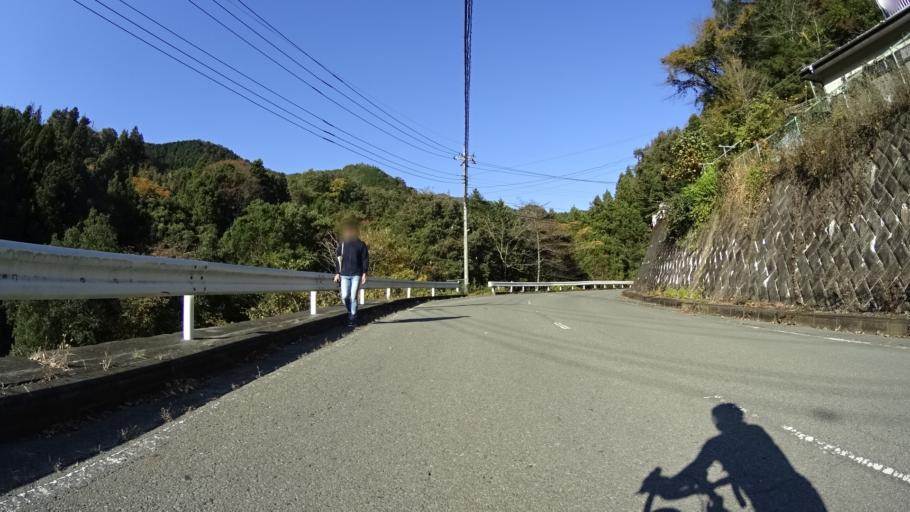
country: JP
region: Yamanashi
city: Uenohara
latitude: 35.6452
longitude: 139.1412
